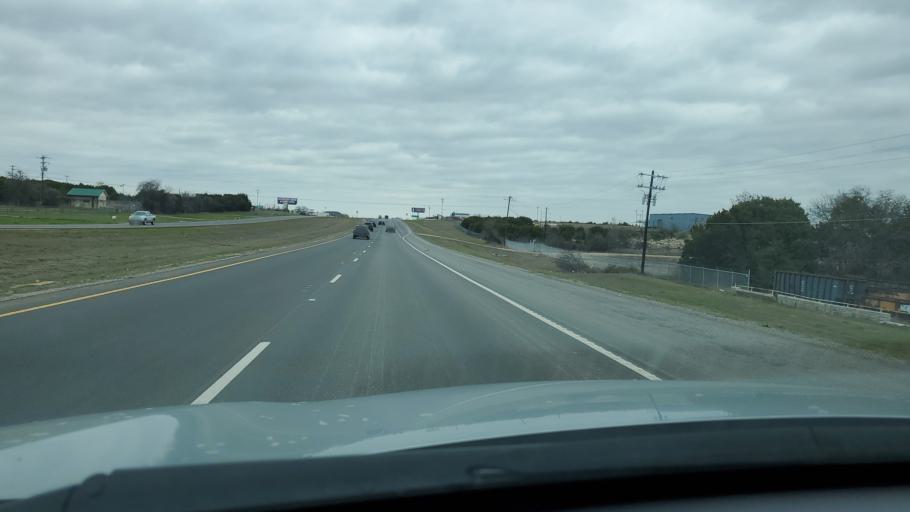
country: US
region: Texas
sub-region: Bell County
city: Killeen
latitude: 31.0123
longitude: -97.7520
